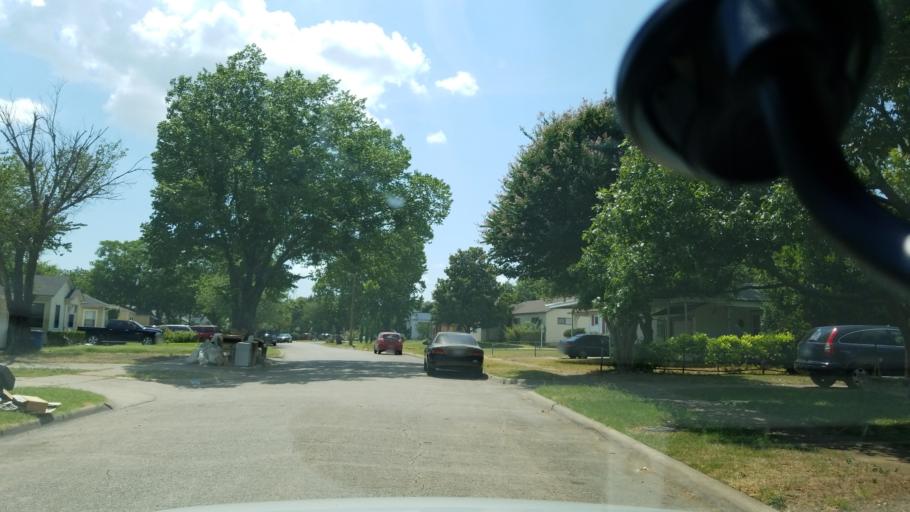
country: US
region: Texas
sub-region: Dallas County
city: Cockrell Hill
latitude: 32.7256
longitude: -96.8806
